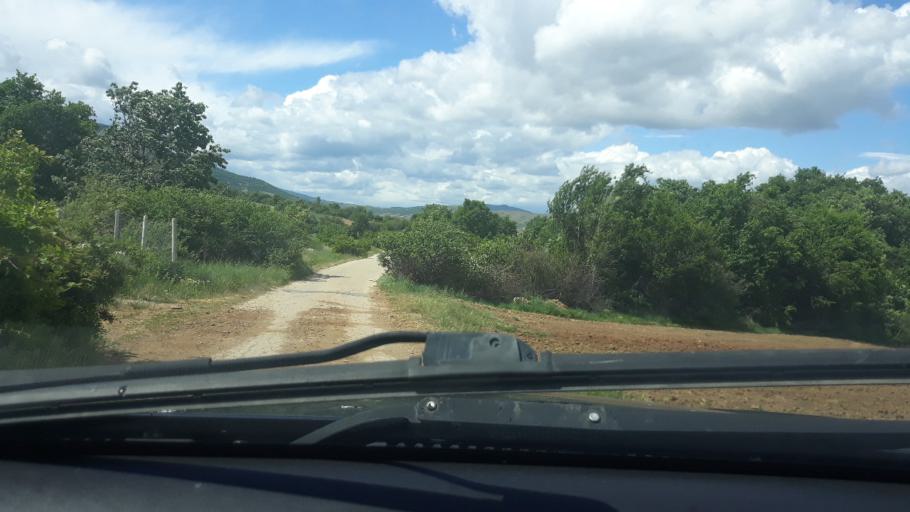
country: MK
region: Krivogastani
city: Krivogashtani
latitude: 41.3294
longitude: 21.3027
